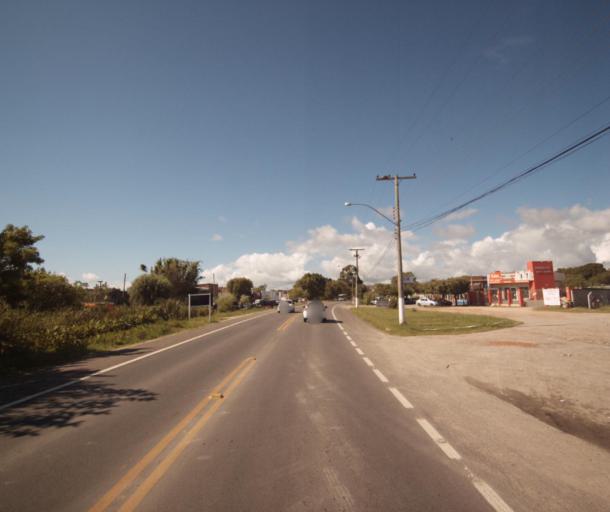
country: BR
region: Rio Grande do Sul
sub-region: Pelotas
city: Pelotas
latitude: -31.7584
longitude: -52.3565
